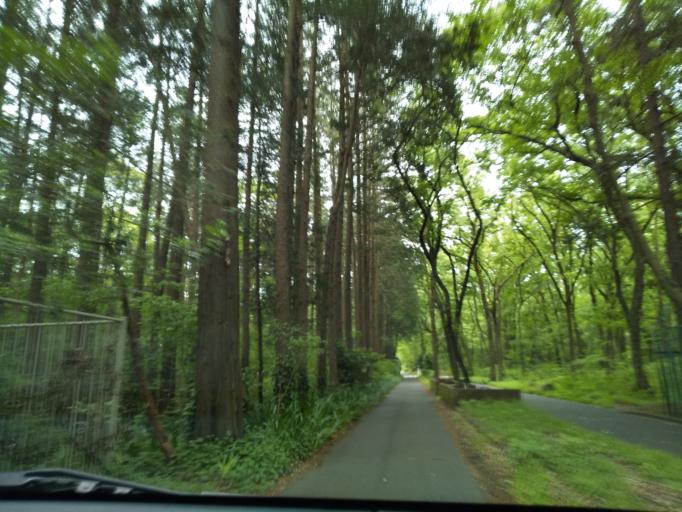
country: JP
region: Tokyo
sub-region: Machida-shi
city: Machida
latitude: 35.5369
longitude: 139.4100
